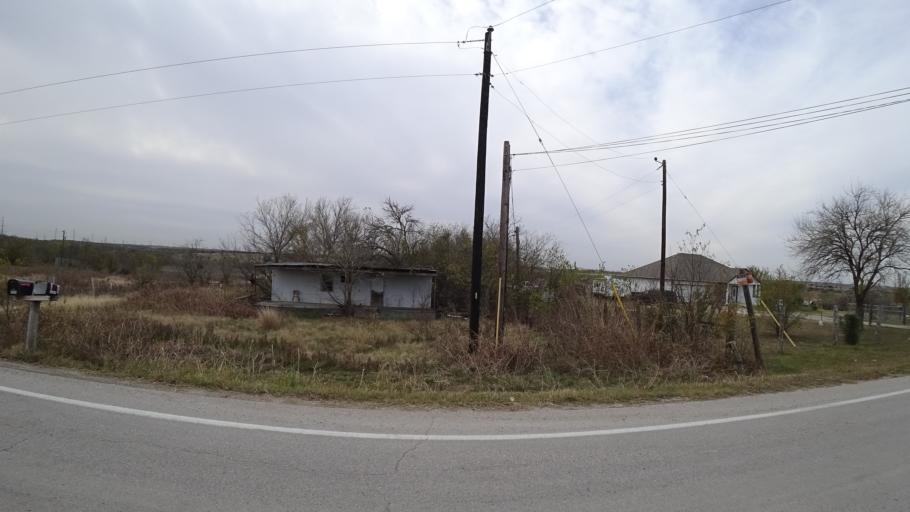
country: US
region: Texas
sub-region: Travis County
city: Onion Creek
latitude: 30.1276
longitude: -97.6802
